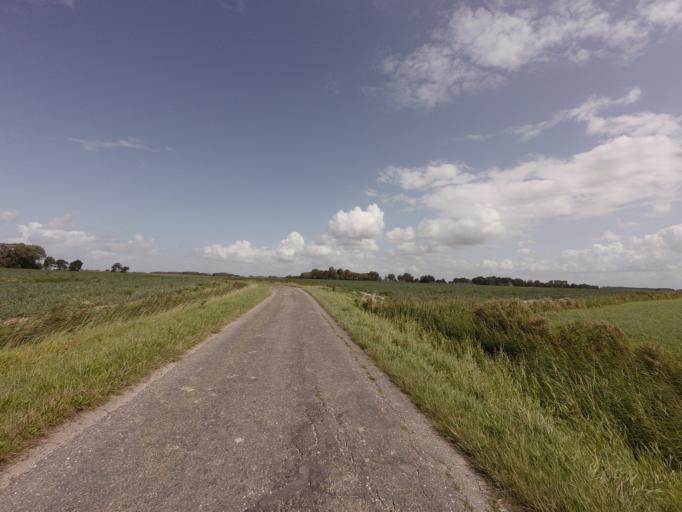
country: NL
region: Friesland
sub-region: Gemeente Harlingen
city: Harlingen
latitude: 53.1206
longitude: 5.4411
